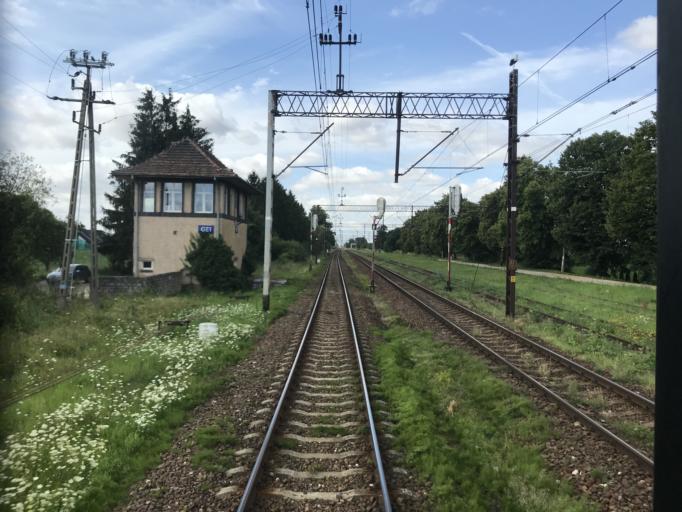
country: PL
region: Warmian-Masurian Voivodeship
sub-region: Powiat elblaski
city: Gronowo Elblaskie
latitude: 54.0916
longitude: 19.3103
